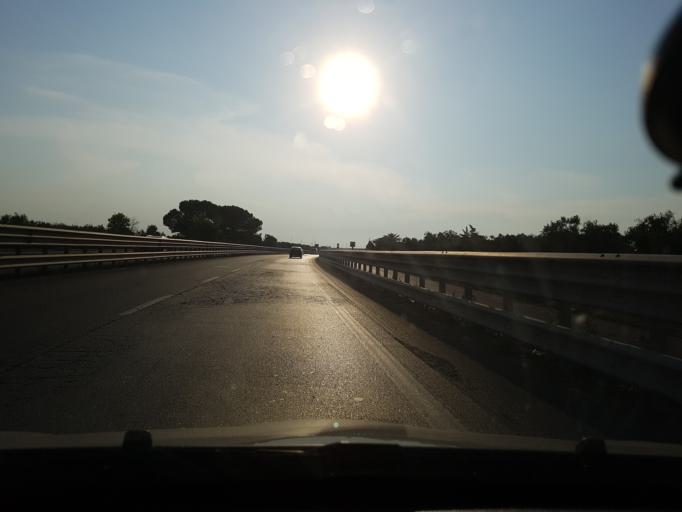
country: IT
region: Apulia
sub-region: Provincia di Foggia
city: Cerignola
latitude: 41.2749
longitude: 15.8737
